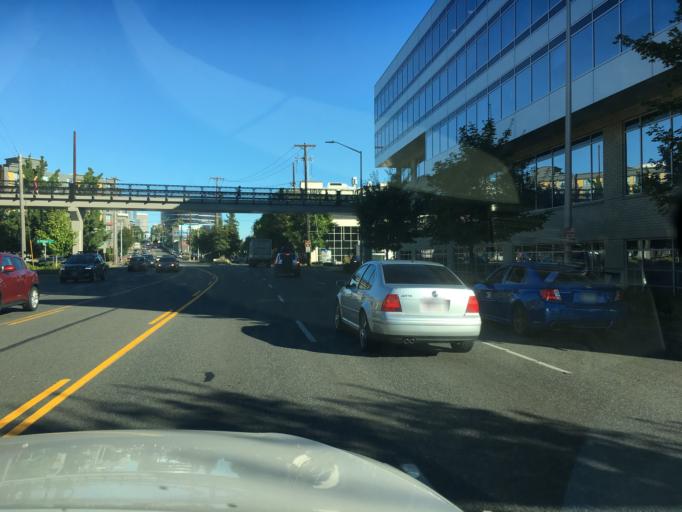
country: US
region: Washington
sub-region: King County
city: Seattle
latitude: 47.6212
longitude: -122.3615
